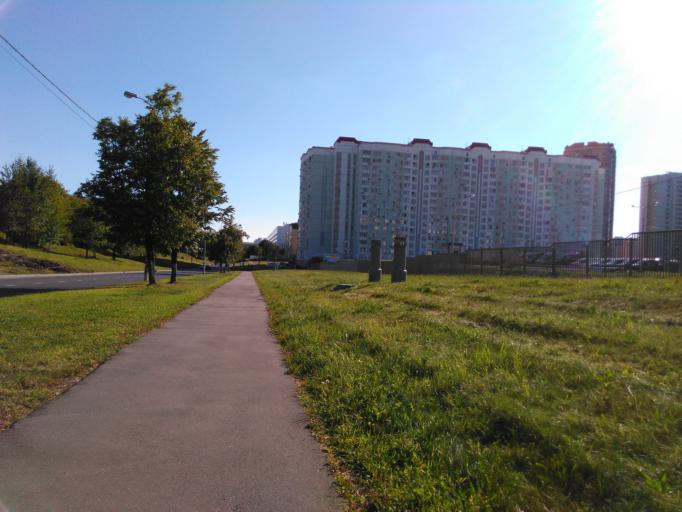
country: RU
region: Moscow
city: Troparevo
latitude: 55.6482
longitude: 37.5063
